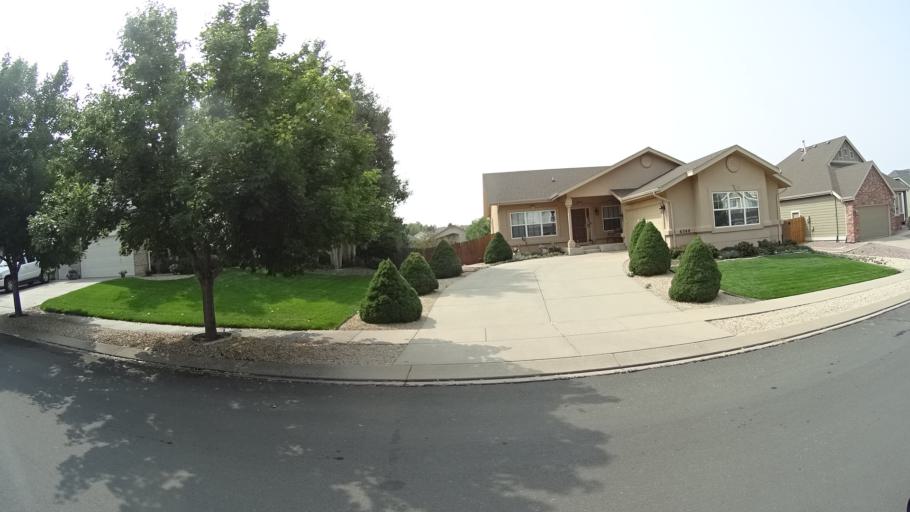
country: US
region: Colorado
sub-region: El Paso County
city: Cimarron Hills
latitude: 38.9225
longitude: -104.7427
